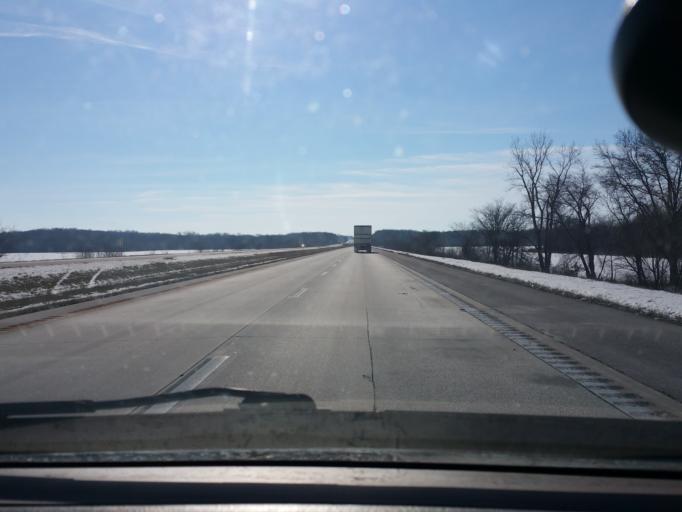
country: US
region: Missouri
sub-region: Daviess County
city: Gallatin
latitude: 40.0336
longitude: -94.0955
